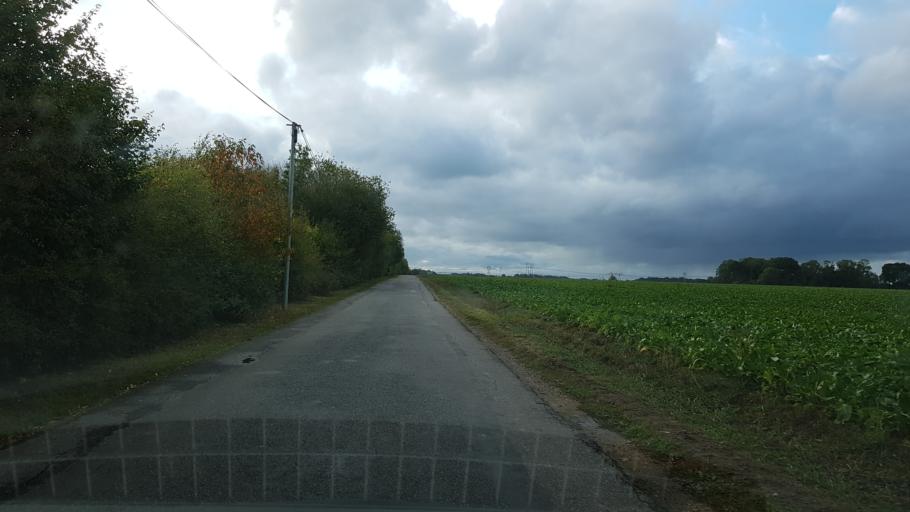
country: FR
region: Ile-de-France
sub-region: Departement de l'Essonne
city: Fontenay-les-Briis
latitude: 48.6327
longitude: 2.1767
